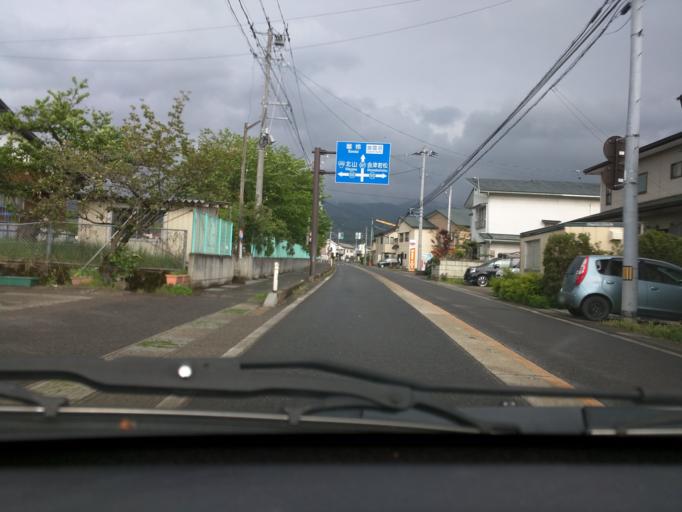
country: JP
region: Fukushima
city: Kitakata
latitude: 37.6429
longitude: 139.9219
